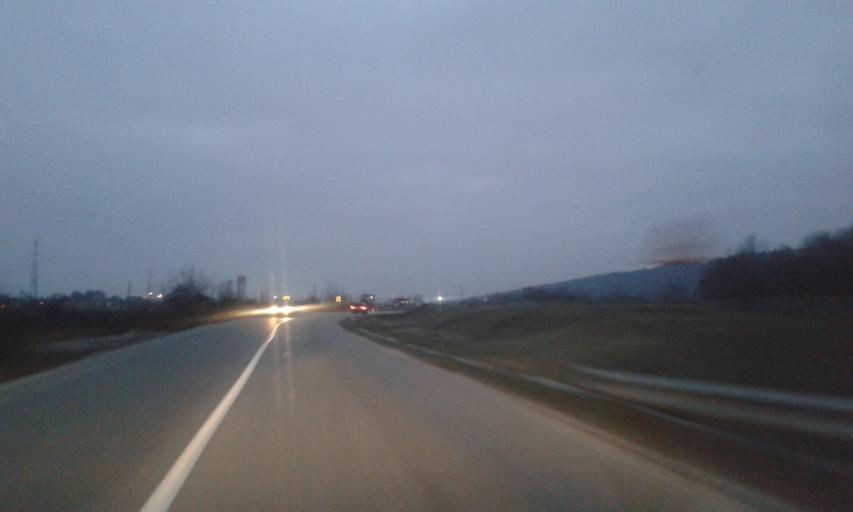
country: RO
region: Gorj
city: Targu Jiu
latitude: 45.0741
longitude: 23.2914
